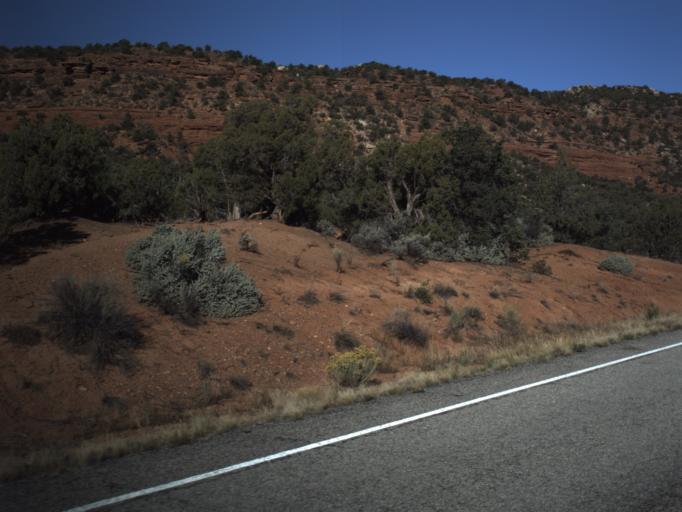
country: US
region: Utah
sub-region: San Juan County
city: Blanding
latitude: 37.5705
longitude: -110.0364
